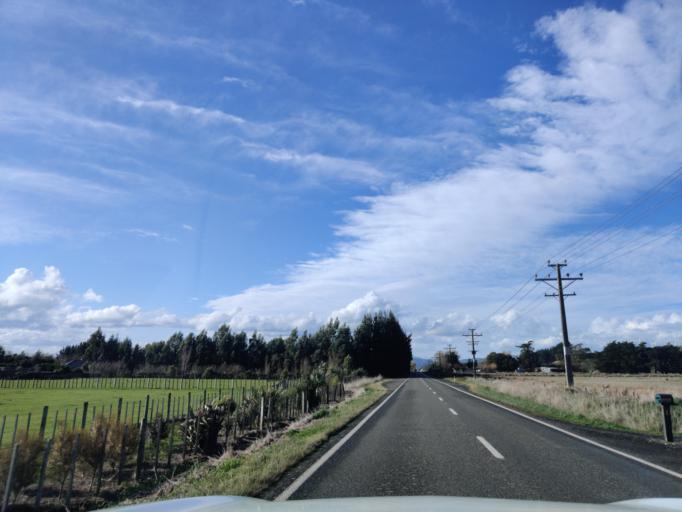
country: NZ
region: Manawatu-Wanganui
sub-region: Palmerston North City
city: Palmerston North
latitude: -40.3612
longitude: 175.6770
